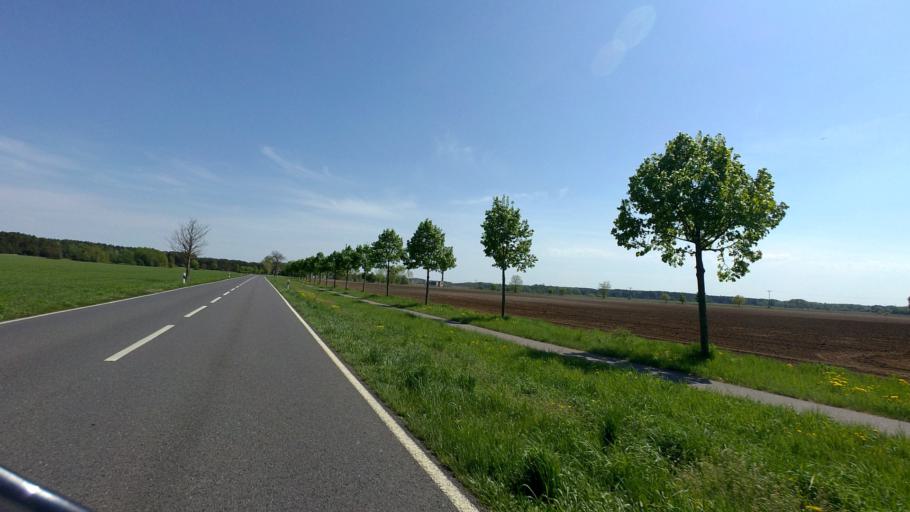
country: DE
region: Brandenburg
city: Schlepzig
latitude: 52.0543
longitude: 13.9748
